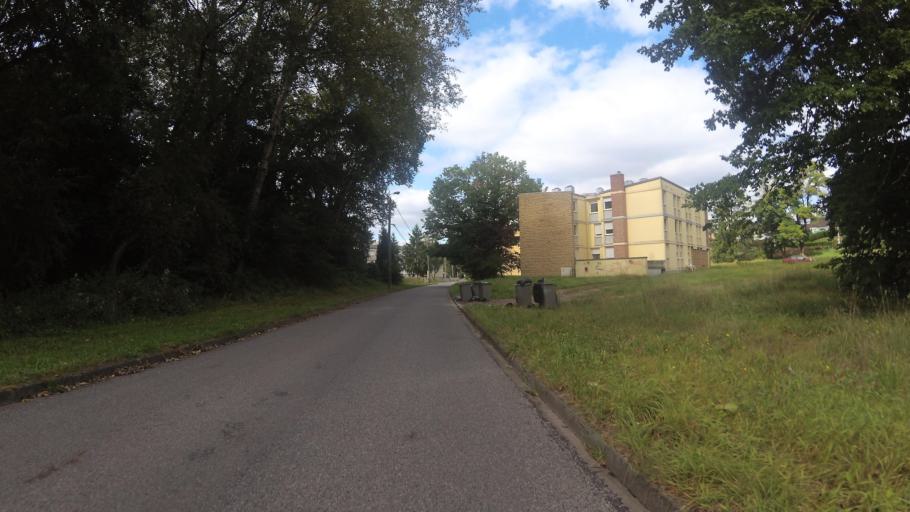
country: FR
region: Lorraine
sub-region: Departement de la Moselle
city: Creutzwald
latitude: 49.2013
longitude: 6.7126
